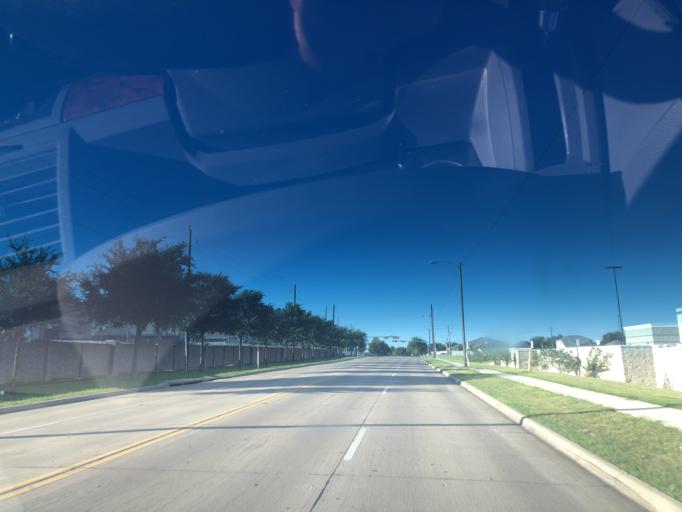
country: US
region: Texas
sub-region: Dallas County
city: Grand Prairie
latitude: 32.7074
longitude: -97.0199
